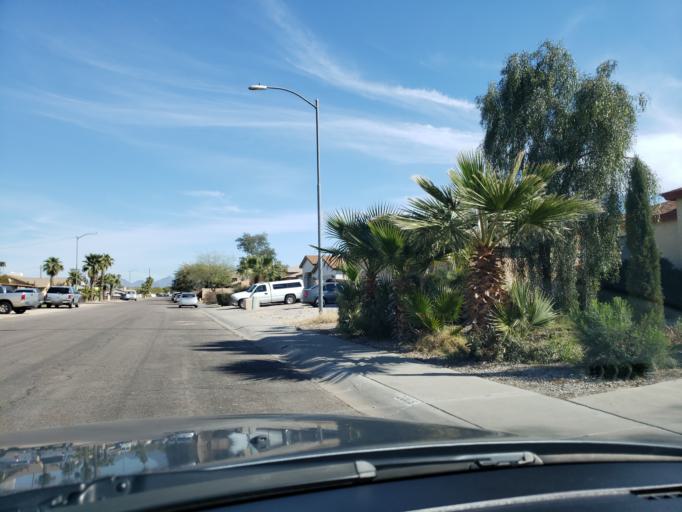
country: US
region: Arizona
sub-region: Maricopa County
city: Paradise Valley
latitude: 33.6418
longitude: -112.0178
